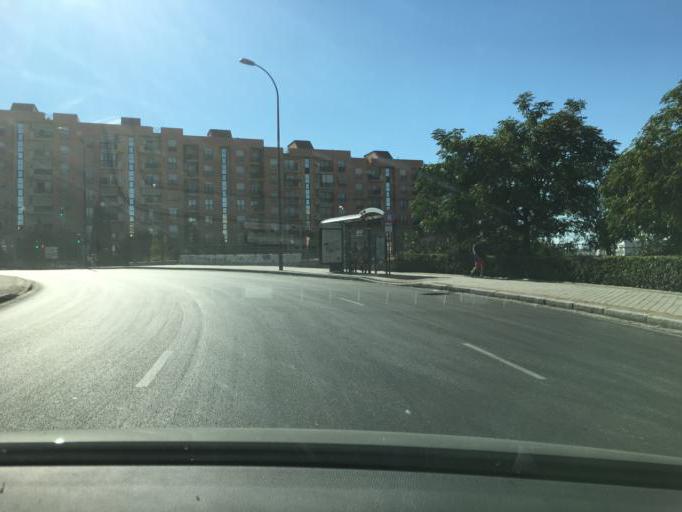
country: ES
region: Andalusia
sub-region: Provincia de Granada
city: Maracena
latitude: 37.1971
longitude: -3.6215
